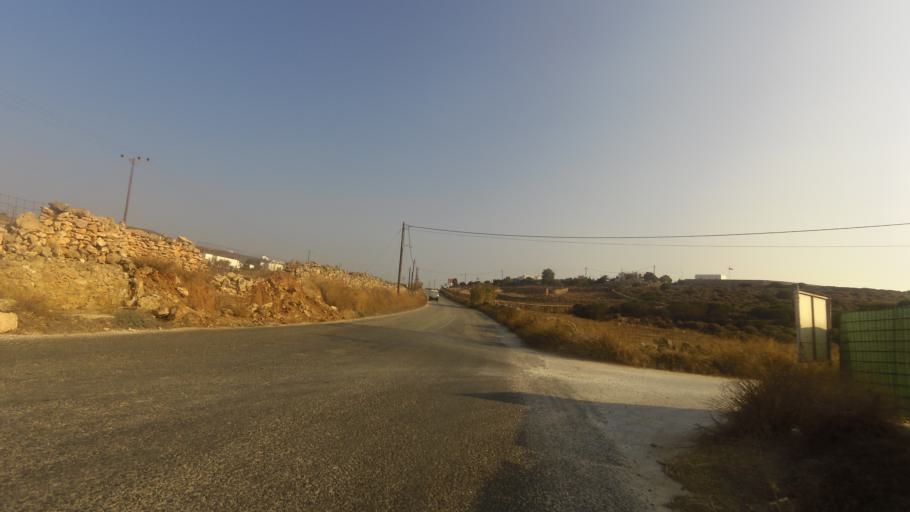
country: GR
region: South Aegean
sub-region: Nomos Kykladon
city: Antiparos
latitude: 37.0306
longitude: 25.0752
